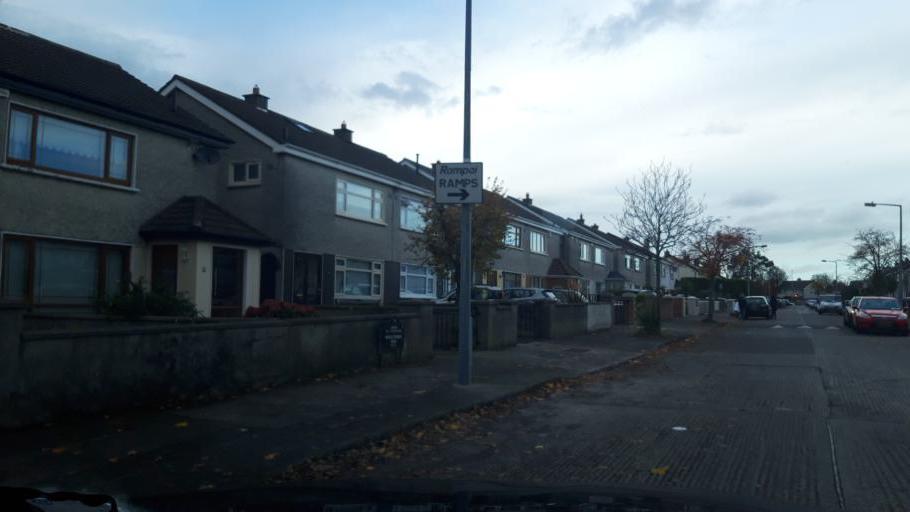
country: IE
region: Leinster
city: Artane
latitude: 53.3826
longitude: -6.2217
